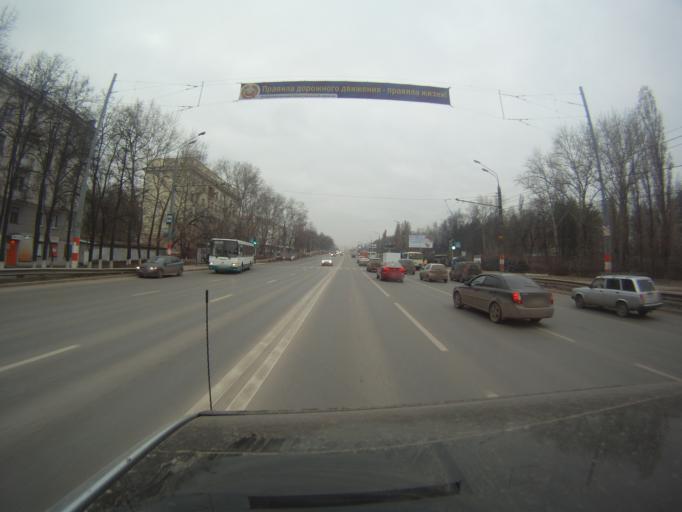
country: RU
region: Nizjnij Novgorod
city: Nizhniy Novgorod
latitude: 56.2962
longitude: 43.9836
